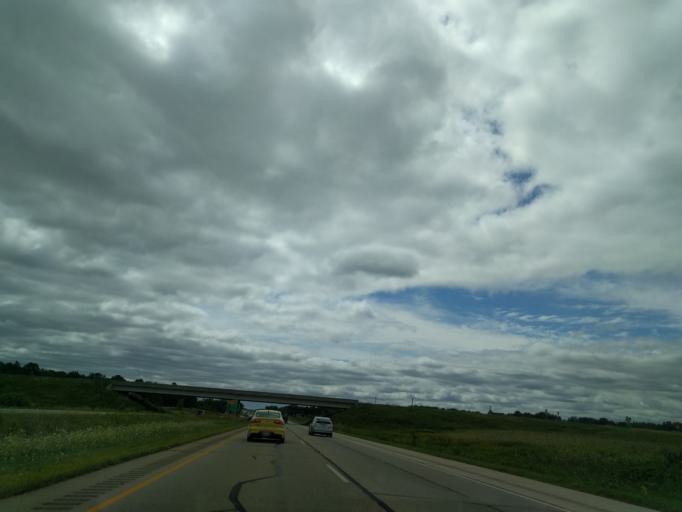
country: US
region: Wisconsin
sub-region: Brown County
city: Suamico
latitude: 44.7661
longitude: -88.0510
